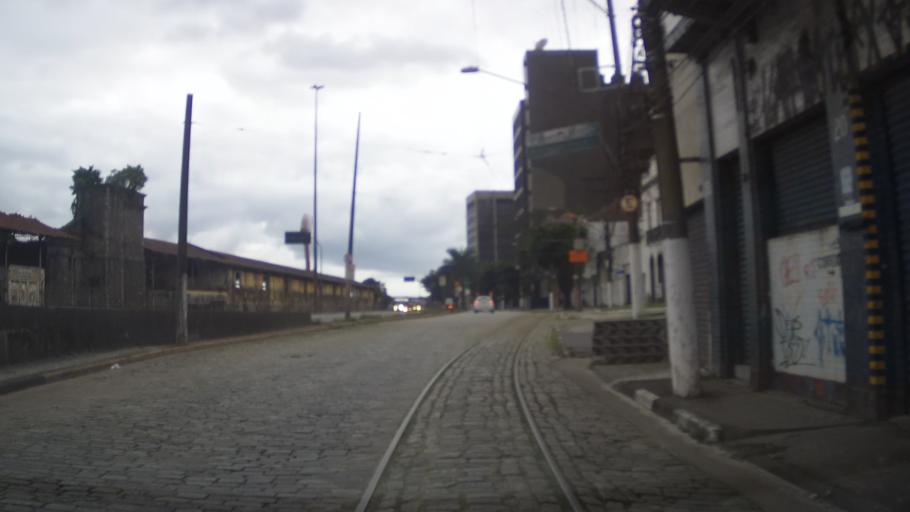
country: BR
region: Sao Paulo
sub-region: Santos
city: Santos
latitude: -23.9319
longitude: -46.3295
